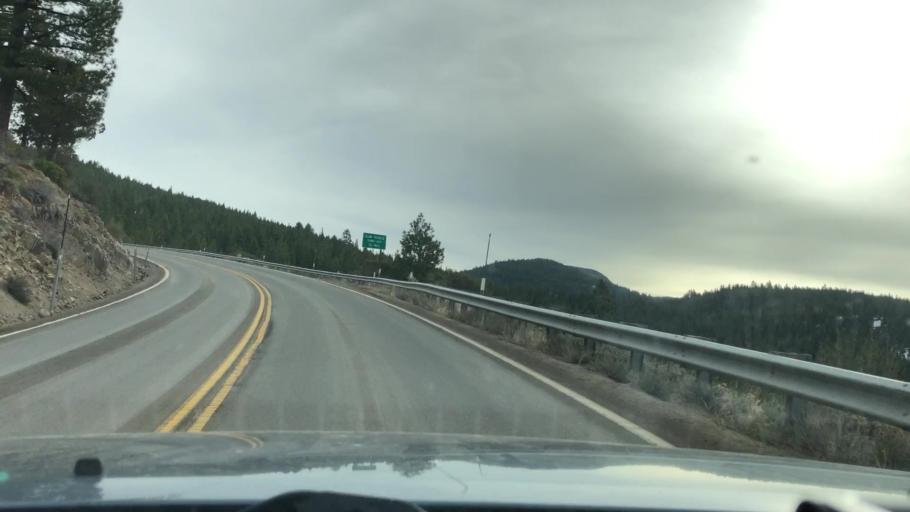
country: US
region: California
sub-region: Nevada County
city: Truckee
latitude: 39.5558
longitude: -120.3405
